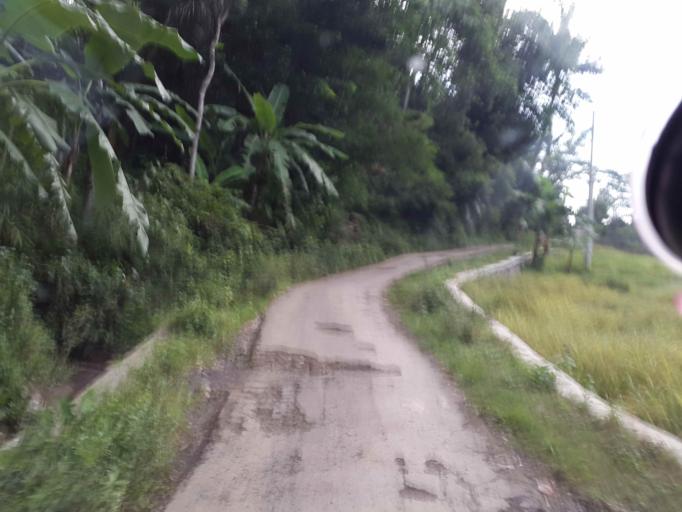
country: ID
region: Central Java
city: Randudongkal
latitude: -7.1237
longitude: 109.3535
